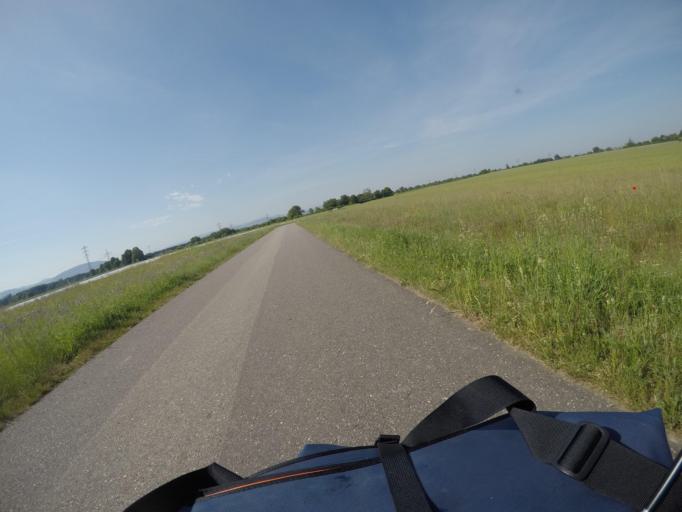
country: DE
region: Baden-Wuerttemberg
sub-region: Karlsruhe Region
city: Durmersheim
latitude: 48.9131
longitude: 8.2771
